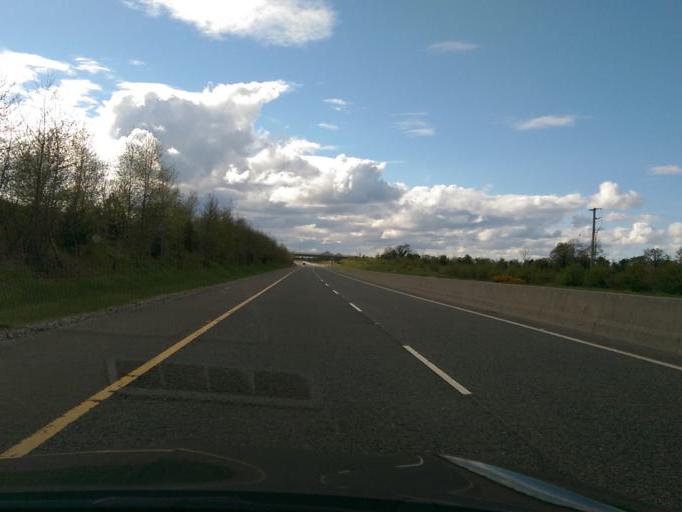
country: IE
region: Leinster
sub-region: An Iarmhi
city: Kilbeggan
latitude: 53.3775
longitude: -7.5596
